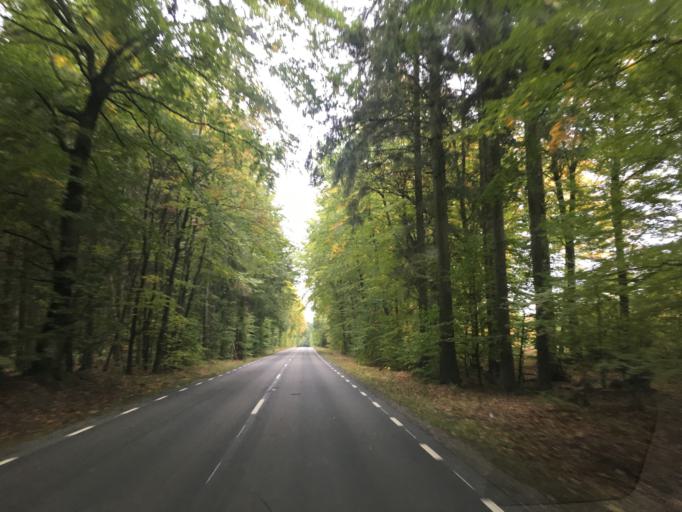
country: SE
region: Skane
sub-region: Simrishamns Kommun
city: Kivik
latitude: 55.6332
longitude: 14.0986
